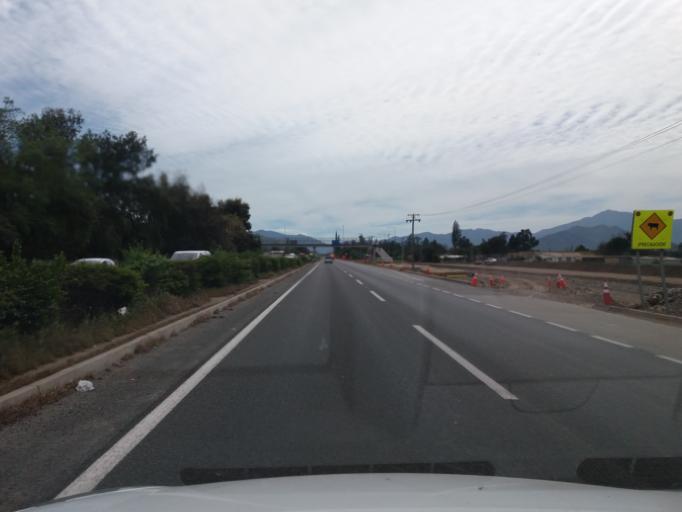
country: CL
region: Valparaiso
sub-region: Provincia de Quillota
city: Hacienda La Calera
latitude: -32.7388
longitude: -71.1987
